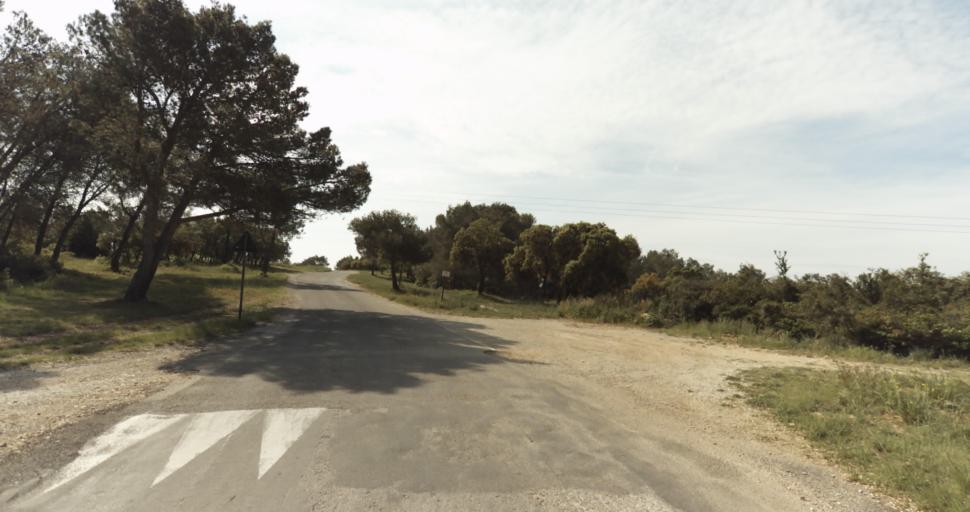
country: FR
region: Languedoc-Roussillon
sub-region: Departement du Gard
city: Poulx
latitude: 43.8803
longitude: 4.3887
